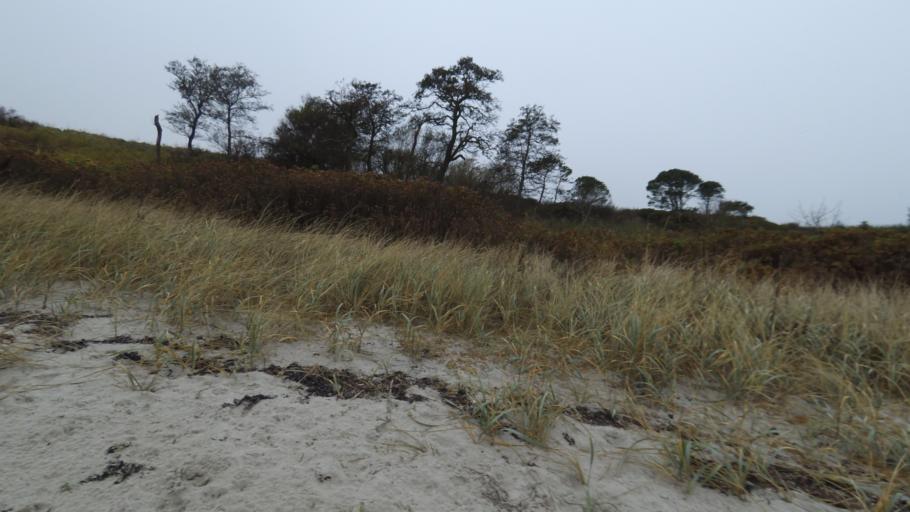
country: DK
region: Central Jutland
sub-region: Arhus Kommune
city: Malling
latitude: 55.9504
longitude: 10.2623
